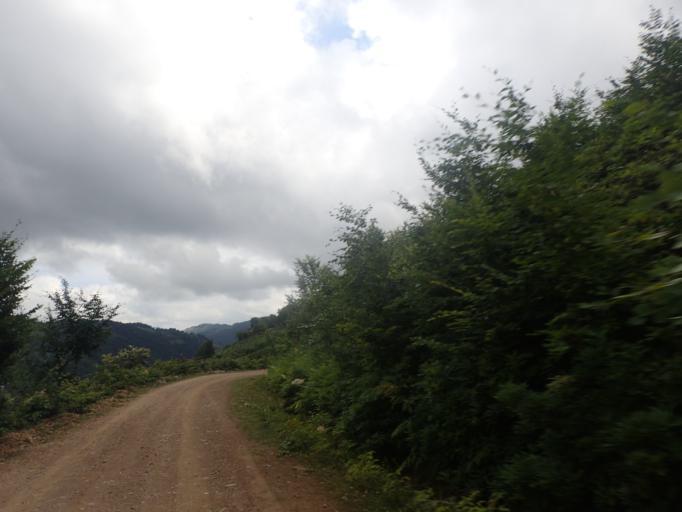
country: TR
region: Ordu
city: Akkus
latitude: 40.8628
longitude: 37.0051
